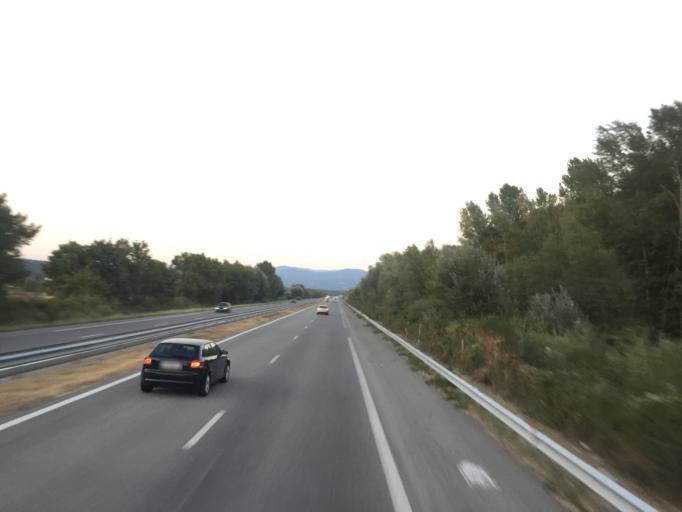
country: FR
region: Provence-Alpes-Cote d'Azur
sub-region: Departement des Alpes-de-Haute-Provence
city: Peyruis
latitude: 44.0220
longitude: 5.9478
